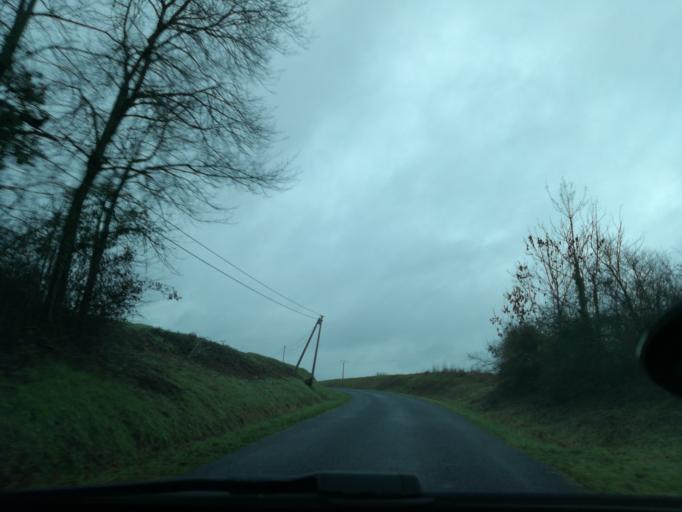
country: FR
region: Lorraine
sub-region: Departement de la Meuse
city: Revigny-sur-Ornain
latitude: 48.8405
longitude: 5.0473
